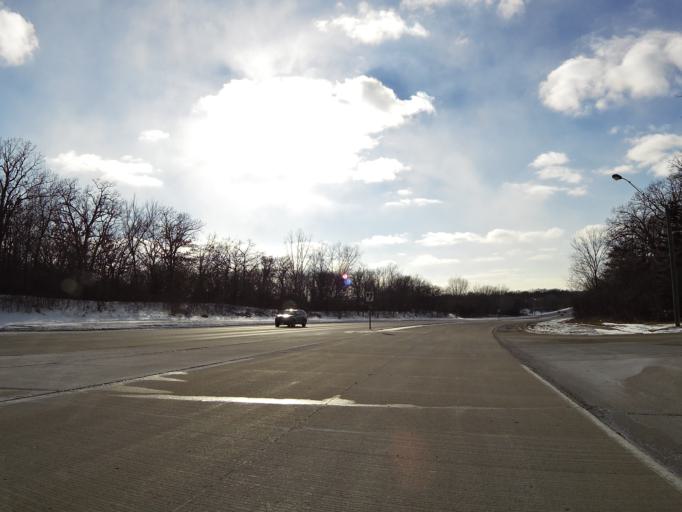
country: US
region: Minnesota
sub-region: Dakota County
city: Apple Valley
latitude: 44.7604
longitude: -93.2022
